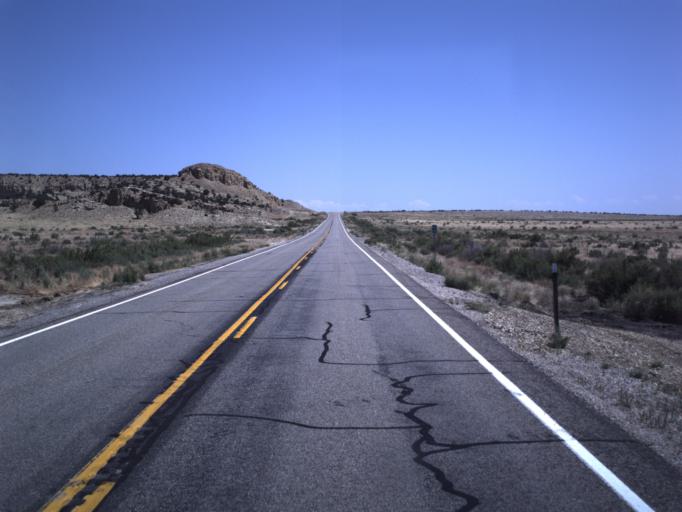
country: US
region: Utah
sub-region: Emery County
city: Ferron
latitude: 38.8182
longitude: -111.3298
